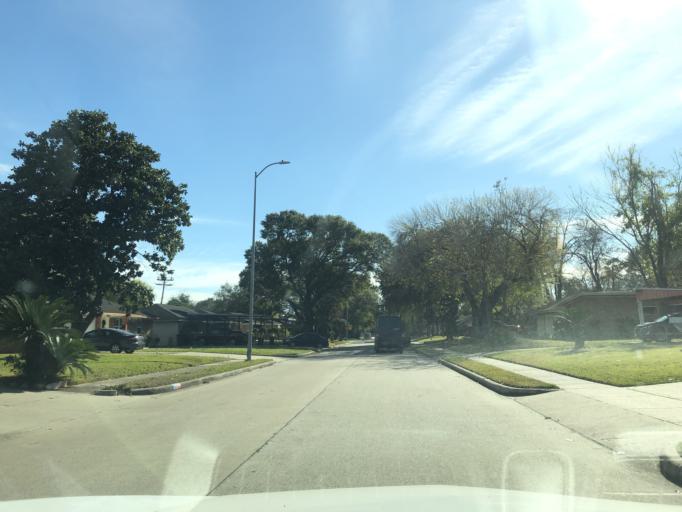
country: US
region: Texas
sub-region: Harris County
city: Bellaire
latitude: 29.6794
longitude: -95.5109
